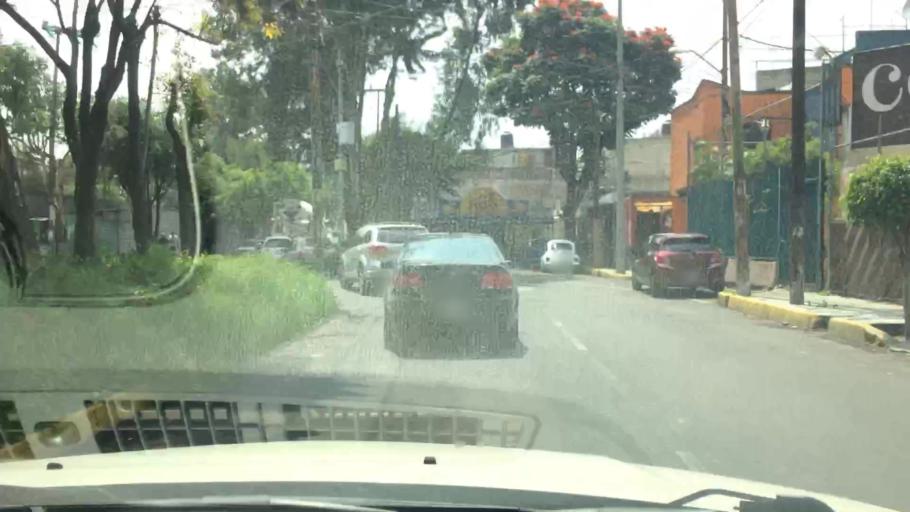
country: MX
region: Mexico City
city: Xochimilco
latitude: 19.2776
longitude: -99.1279
